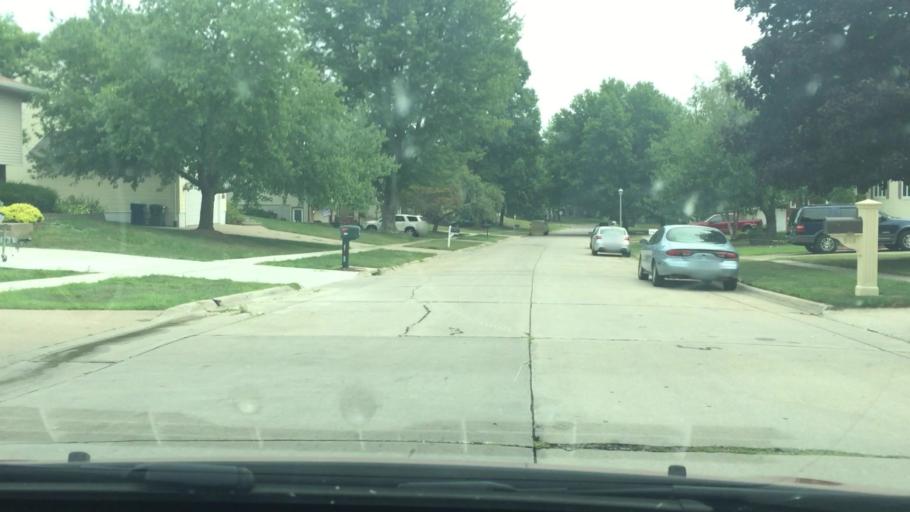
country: US
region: Iowa
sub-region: Muscatine County
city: Muscatine
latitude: 41.4417
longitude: -91.0537
